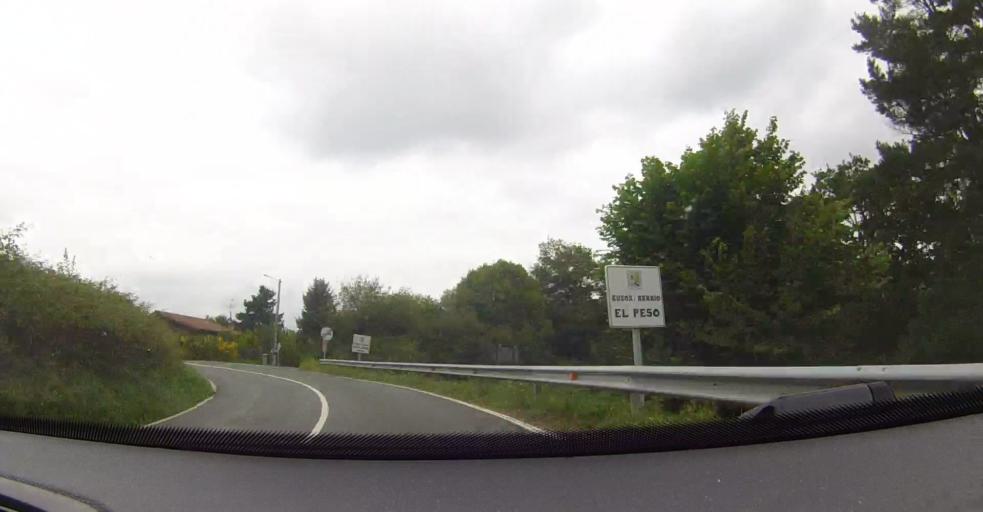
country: ES
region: Basque Country
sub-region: Bizkaia
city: Balmaseda
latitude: 43.2441
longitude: -3.2349
